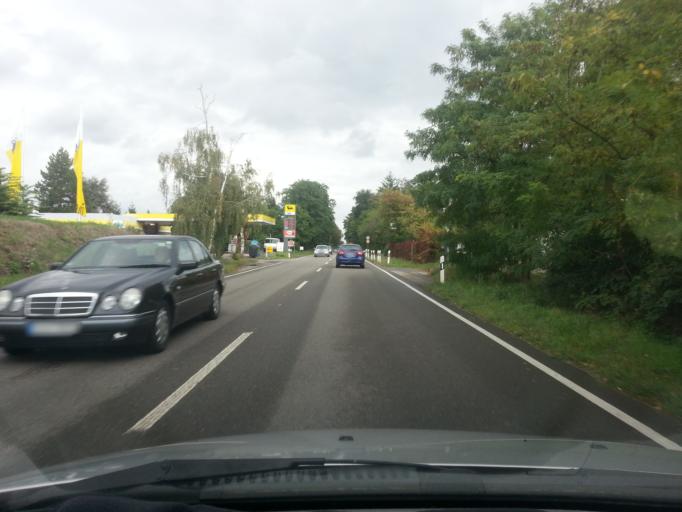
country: DE
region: Rheinland-Pfalz
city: Birkenheide
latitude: 49.4801
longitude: 8.2670
